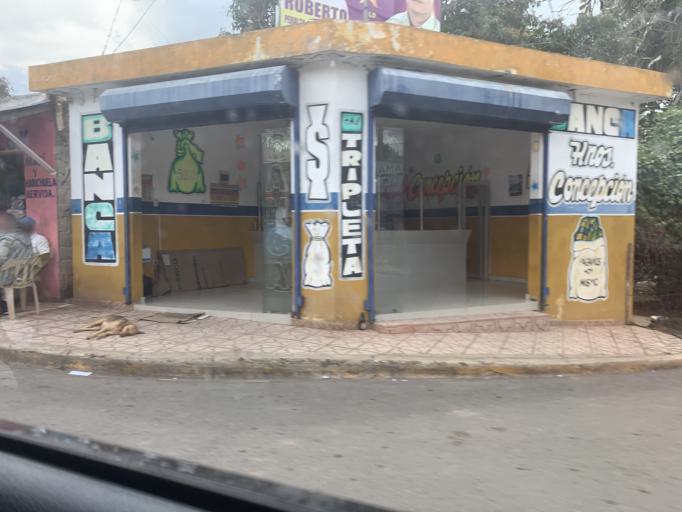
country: DO
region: Monte Plata
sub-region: Yamasa
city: Yamasa
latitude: 18.7711
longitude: -70.0189
